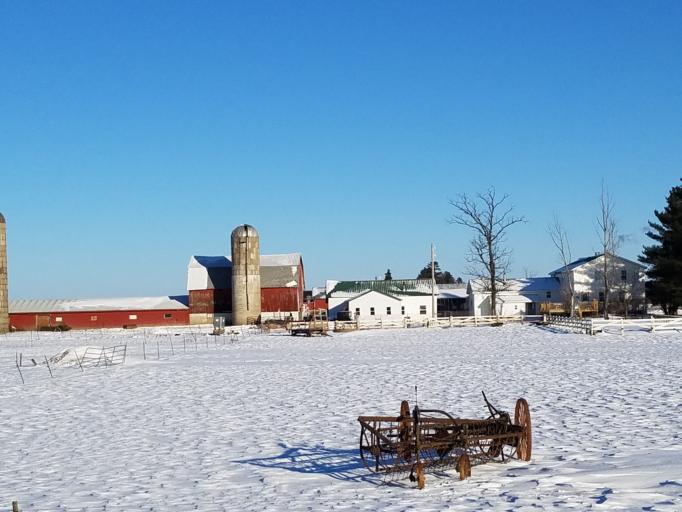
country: US
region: Wisconsin
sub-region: Clark County
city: Loyal
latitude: 44.6403
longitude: -90.3983
